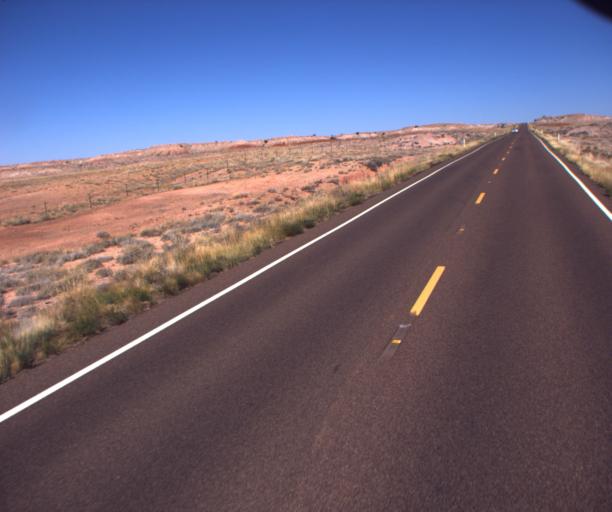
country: US
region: Arizona
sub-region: Navajo County
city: Dilkon
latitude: 35.2017
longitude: -110.4398
